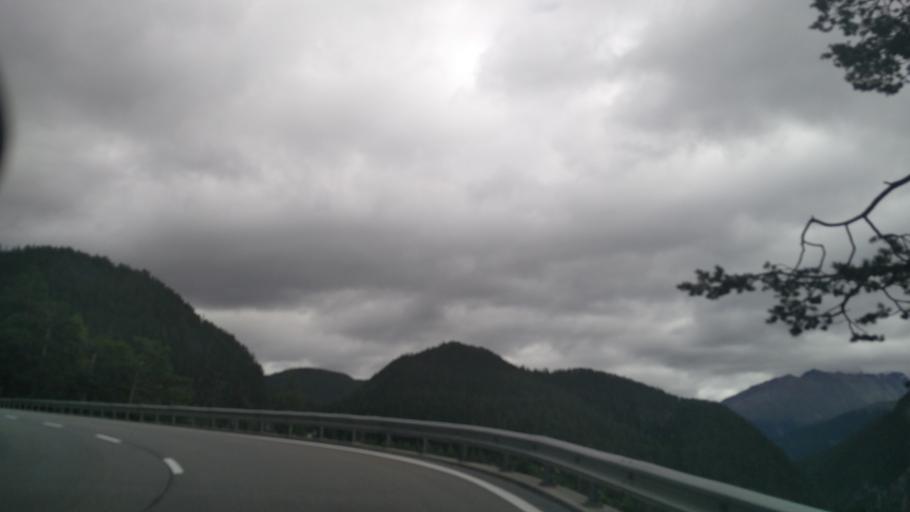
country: CH
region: Grisons
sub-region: Inn District
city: Zernez
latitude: 46.6896
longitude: 10.1388
